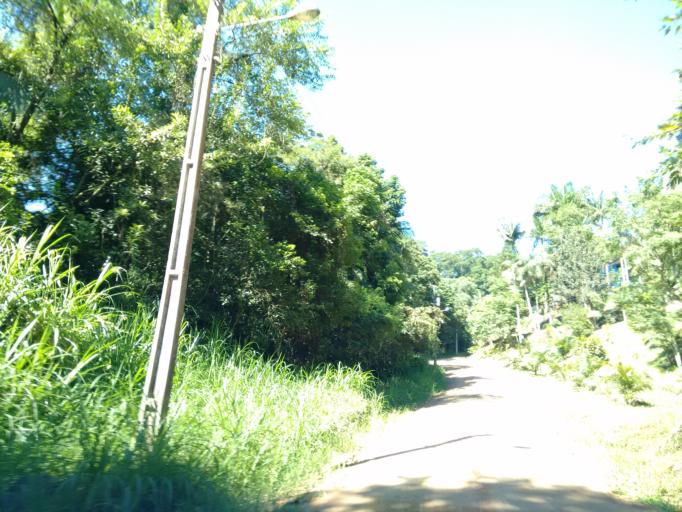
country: BR
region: Santa Catarina
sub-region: Pomerode
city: Pomerode
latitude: -26.7530
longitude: -49.1871
